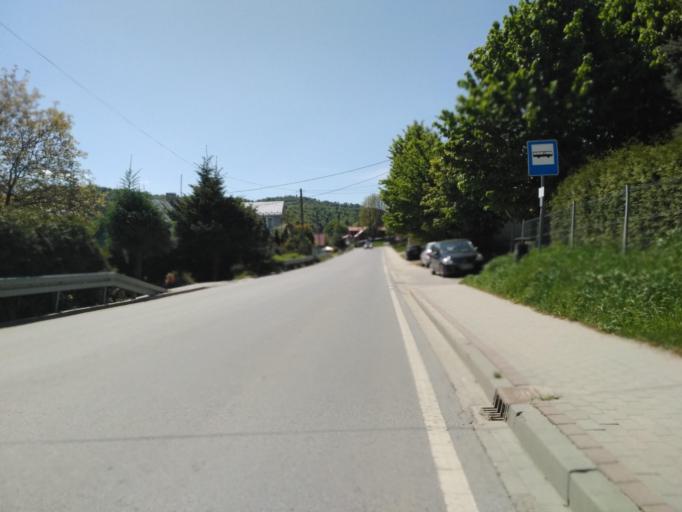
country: PL
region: Subcarpathian Voivodeship
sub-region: Powiat krosnienski
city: Iwonicz-Zdroj
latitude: 49.5726
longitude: 21.7928
